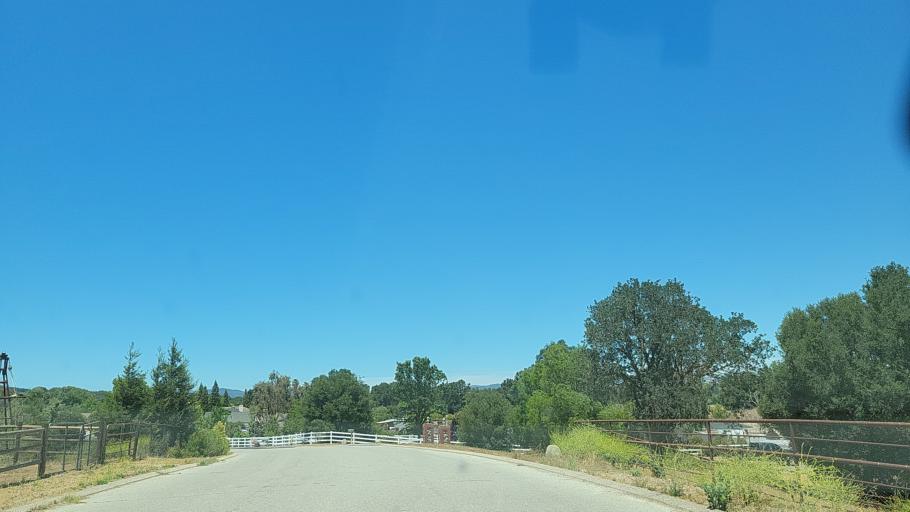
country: US
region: California
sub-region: San Luis Obispo County
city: Atascadero
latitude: 35.5178
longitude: -120.6801
